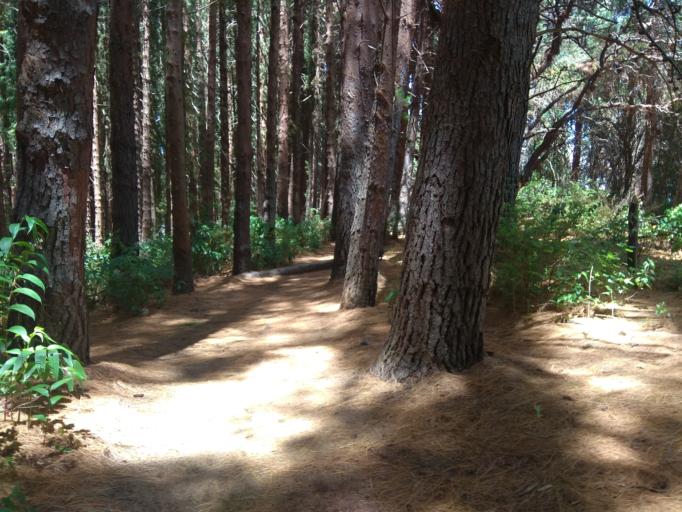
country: CR
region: Cartago
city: Cot
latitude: 9.9568
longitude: -83.8748
